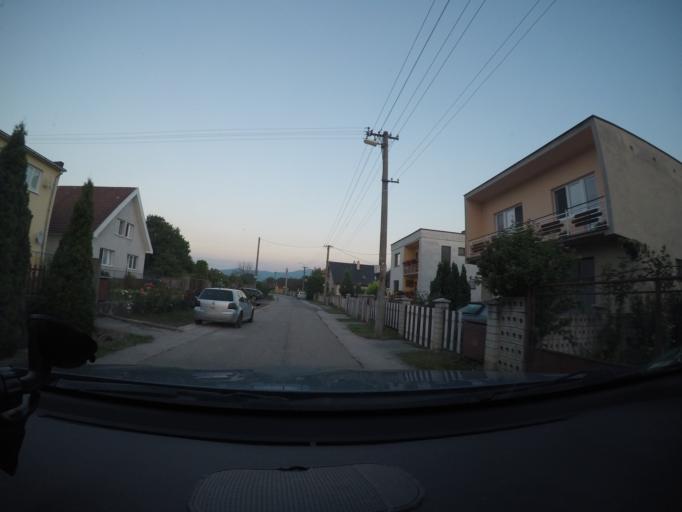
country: SK
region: Trenciansky
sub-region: Okres Trencin
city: Trencin
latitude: 48.8494
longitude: 17.9307
